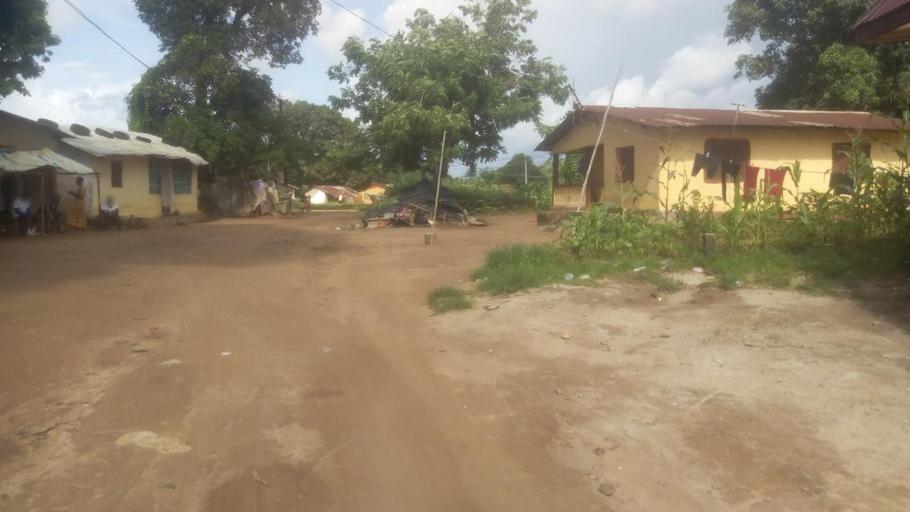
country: SL
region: Northern Province
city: Masoyila
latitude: 8.6095
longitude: -13.1904
